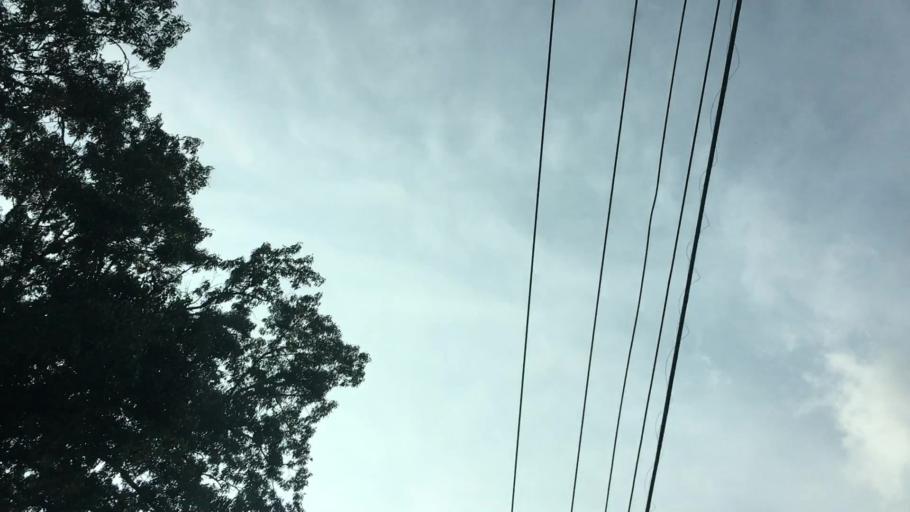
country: US
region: Alabama
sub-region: Bibb County
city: Woodstock
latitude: 33.2206
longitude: -87.1198
